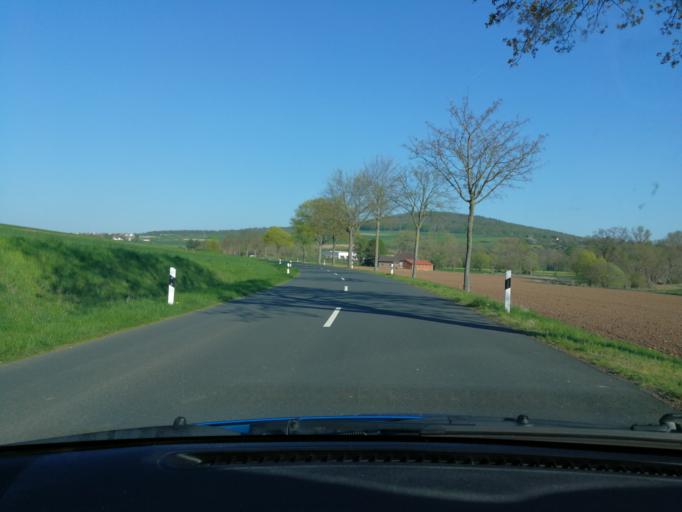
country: DE
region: Lower Saxony
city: Adelebsen
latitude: 51.5476
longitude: 9.7503
